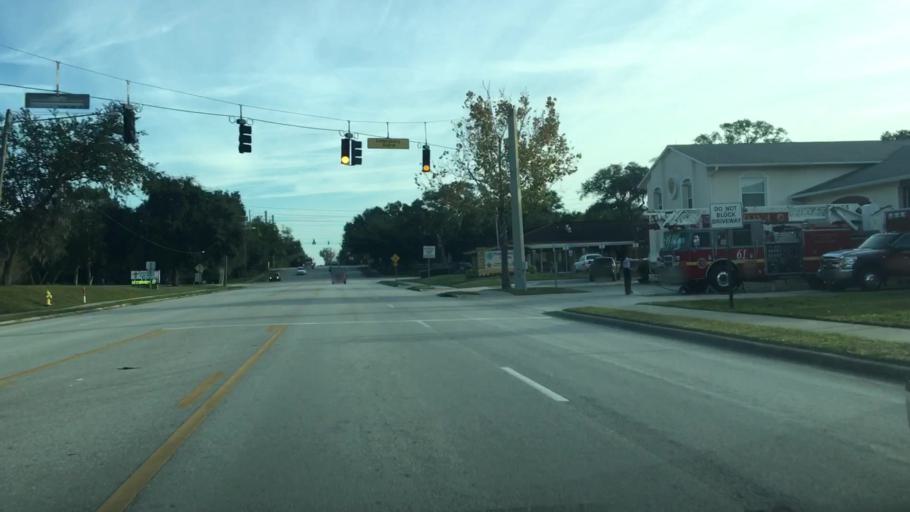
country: US
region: Florida
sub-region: Volusia County
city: Deltona
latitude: 28.9064
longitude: -81.2263
